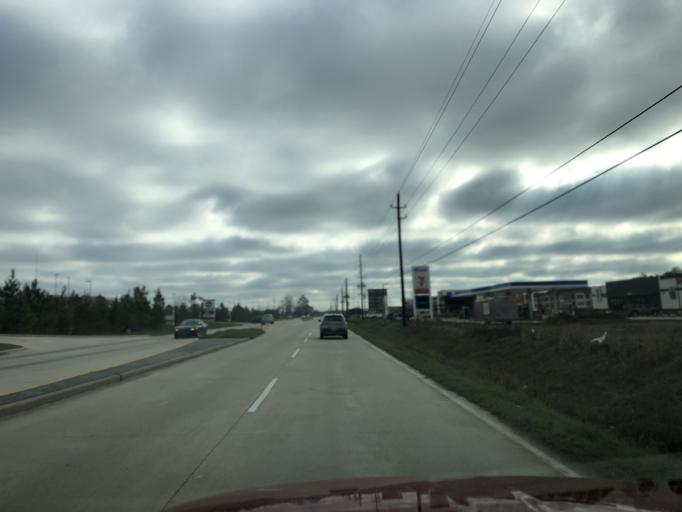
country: US
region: Texas
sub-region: Harris County
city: Spring
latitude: 30.0829
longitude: -95.4503
